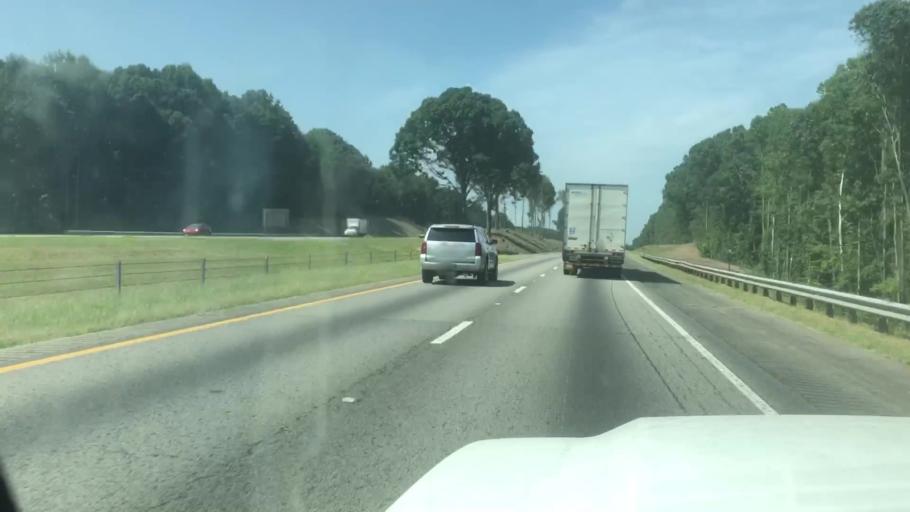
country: US
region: Georgia
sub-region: Jackson County
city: Jefferson
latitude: 34.1388
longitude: -83.6683
